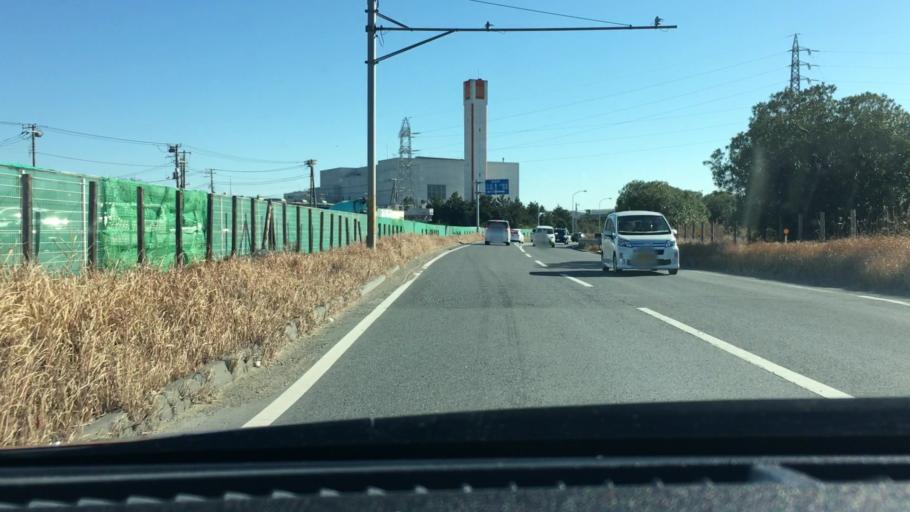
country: JP
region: Chiba
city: Kisarazu
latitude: 35.3715
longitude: 139.9088
